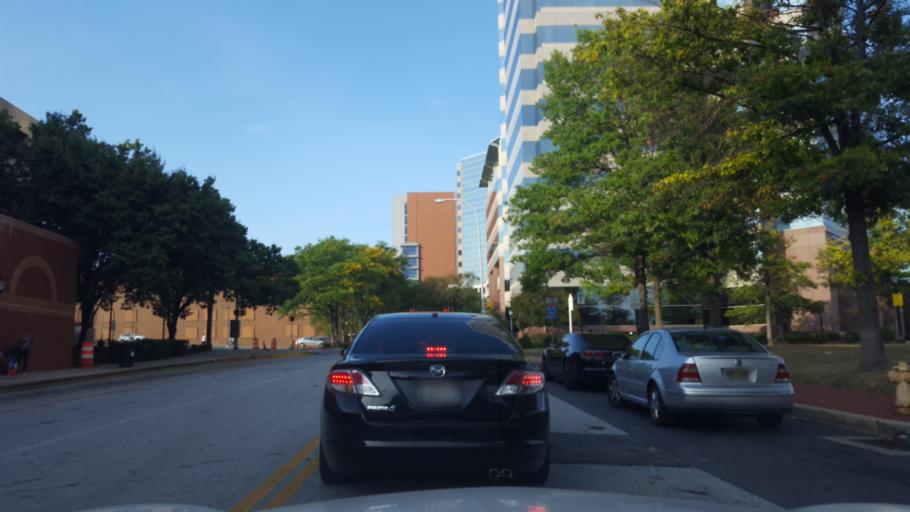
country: US
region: Delaware
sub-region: New Castle County
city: Wilmington
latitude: 39.7376
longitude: -75.5511
